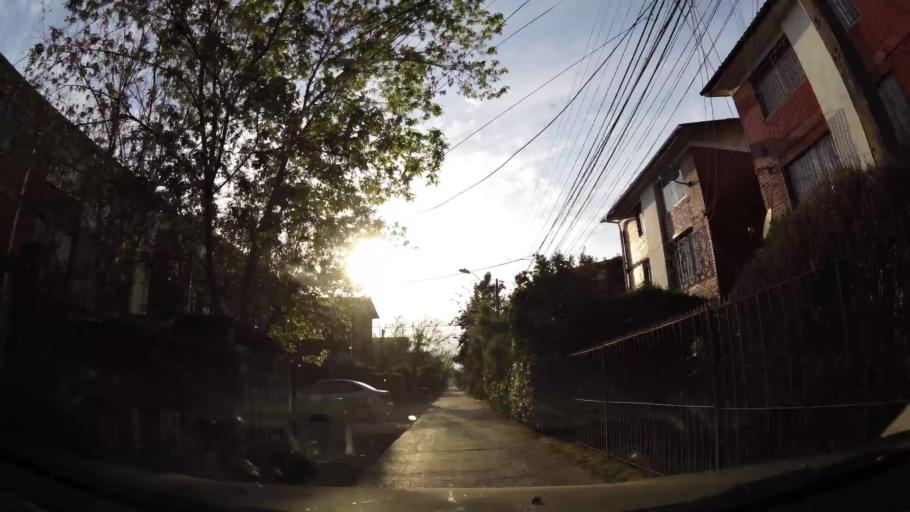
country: CL
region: Santiago Metropolitan
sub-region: Provincia de Santiago
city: Villa Presidente Frei, Nunoa, Santiago, Chile
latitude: -33.5202
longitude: -70.5866
